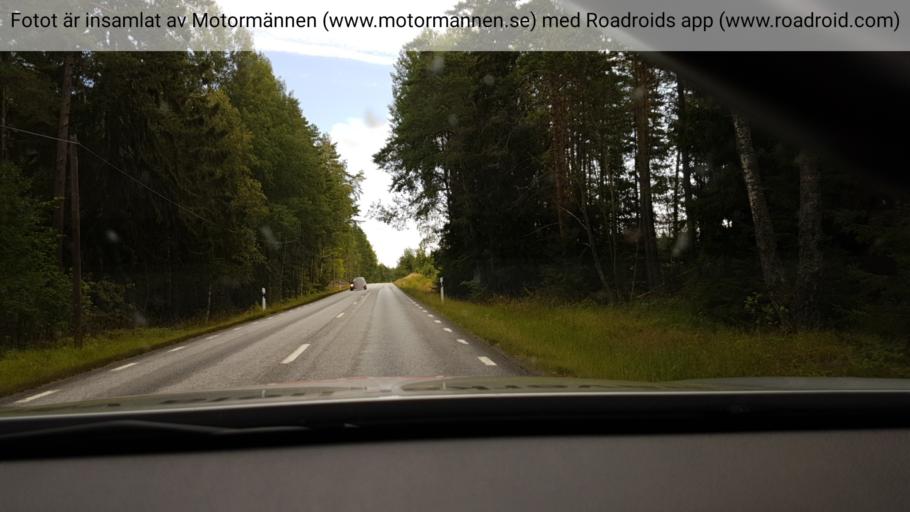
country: SE
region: Stockholm
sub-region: Vaxholms Kommun
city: Vaxholm
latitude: 59.5492
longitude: 18.5343
